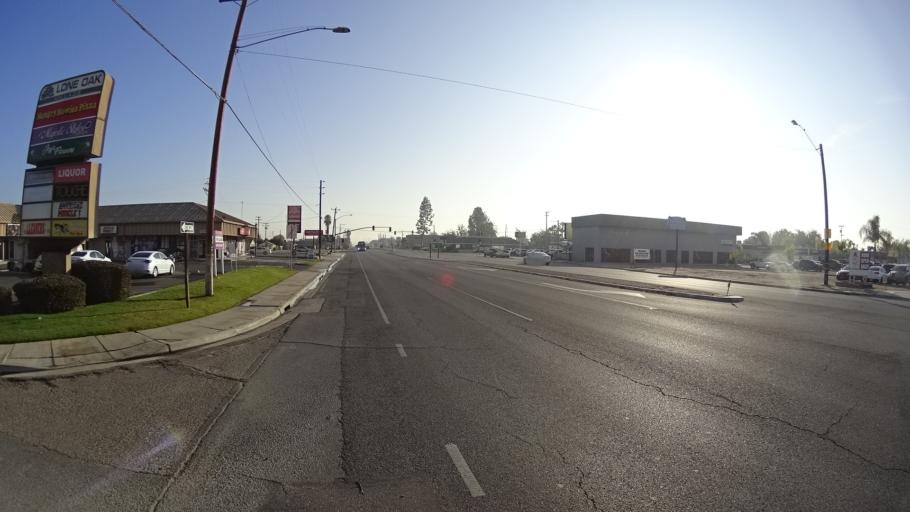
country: US
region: California
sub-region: Kern County
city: Greenacres
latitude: 35.3835
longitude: -119.1203
